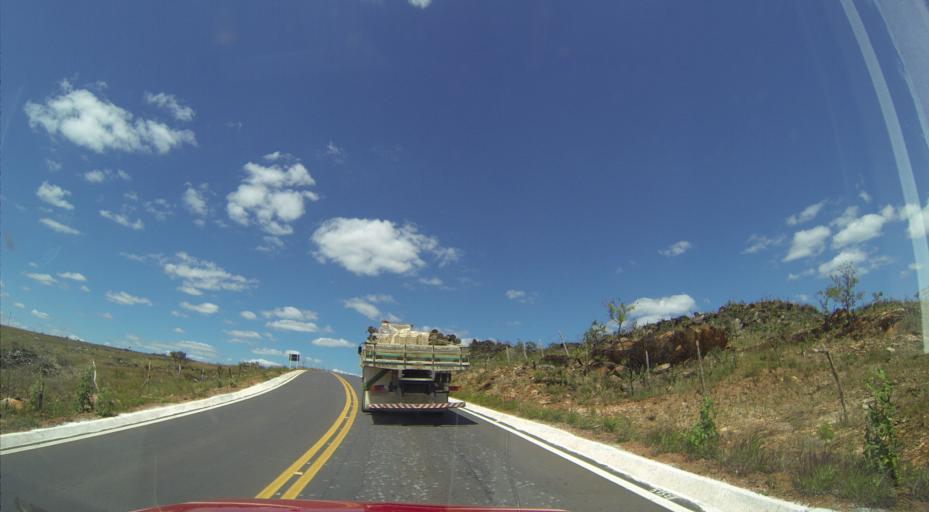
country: BR
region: Minas Gerais
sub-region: Conceicao Do Mato Dentro
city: Conceicao do Mato Dentro
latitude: -19.2859
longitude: -43.5755
